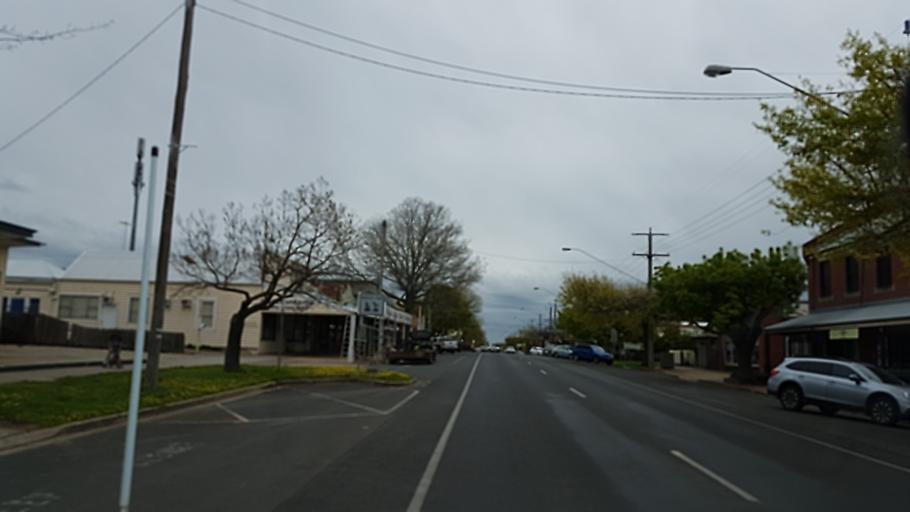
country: AU
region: Victoria
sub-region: Moorabool
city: Bacchus Marsh
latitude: -37.6001
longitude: 144.2275
